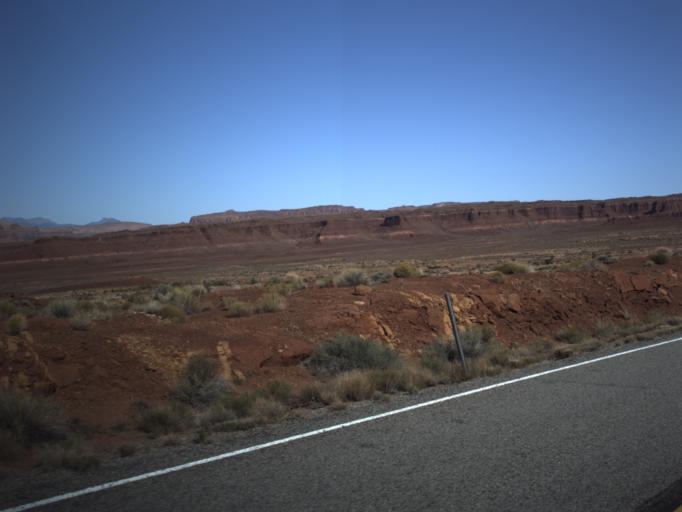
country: US
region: Utah
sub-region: San Juan County
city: Blanding
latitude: 37.8272
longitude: -110.3587
